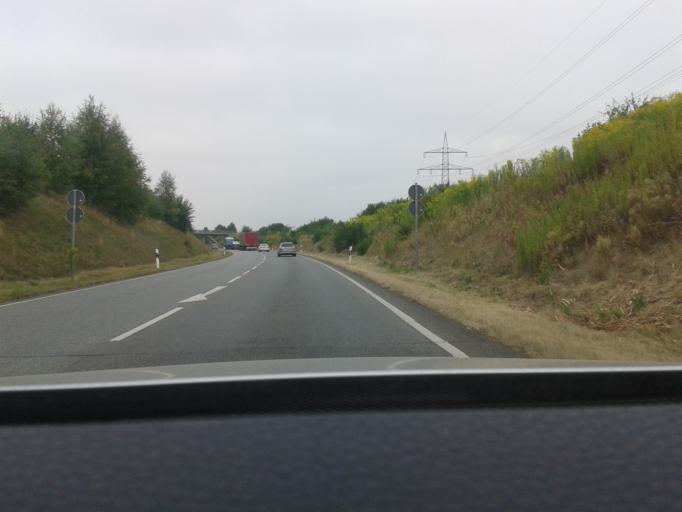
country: DE
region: Saxony
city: Kreischa
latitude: 50.9953
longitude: 13.7789
